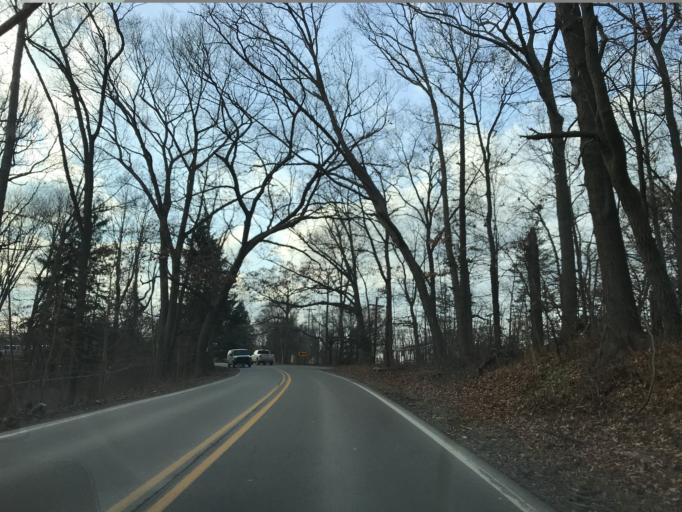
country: US
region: Michigan
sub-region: Oakland County
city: South Lyon
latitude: 42.4679
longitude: -83.7010
